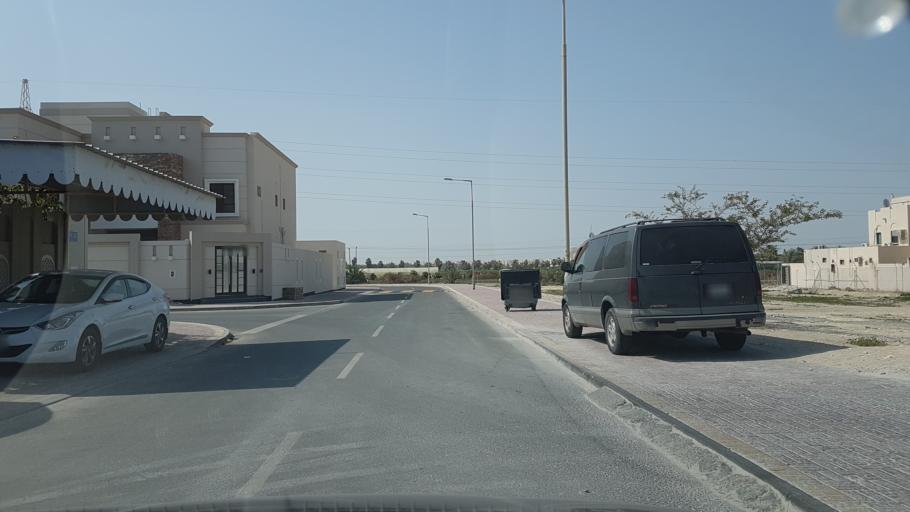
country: BH
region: Northern
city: Madinat `Isa
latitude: 26.1686
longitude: 50.5371
